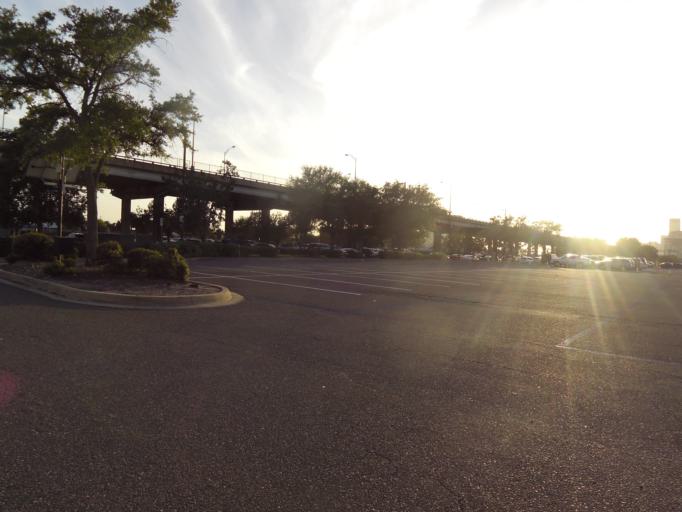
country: US
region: Florida
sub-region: Duval County
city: Jacksonville
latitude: 30.3219
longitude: -81.6393
